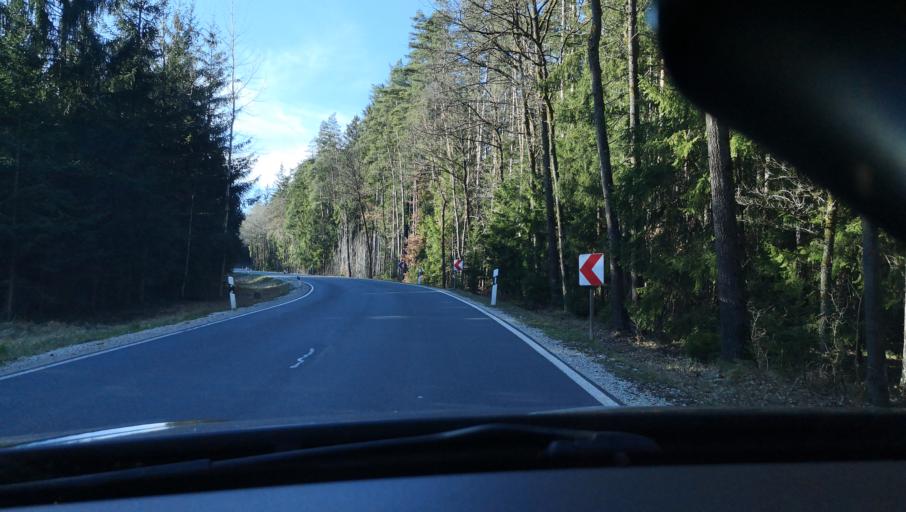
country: DE
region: Bavaria
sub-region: Upper Franconia
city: Michelau
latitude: 50.1922
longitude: 11.1123
